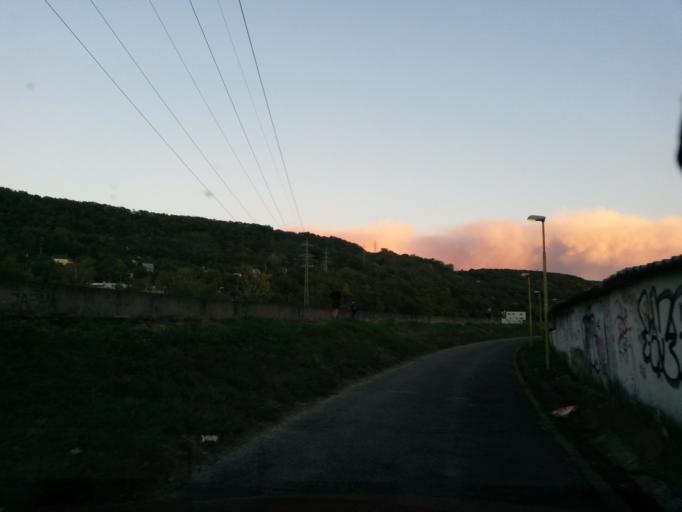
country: SK
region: Kosicky
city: Kosice
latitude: 48.6982
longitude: 21.2834
